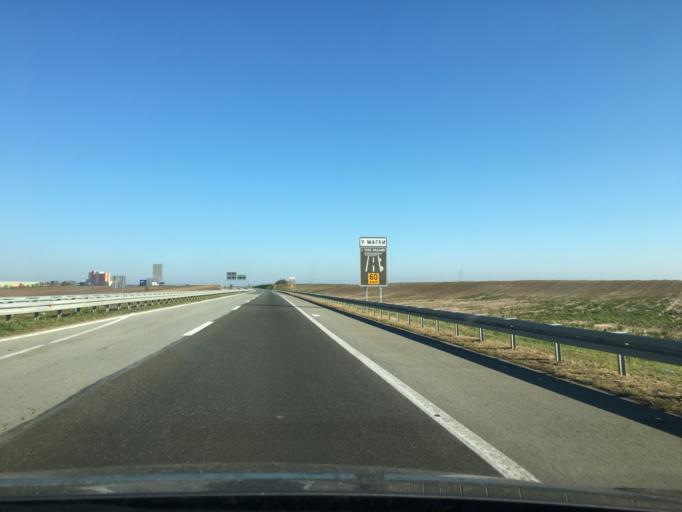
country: RS
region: Autonomna Pokrajina Vojvodina
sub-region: Severnobacki Okrug
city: Mali Igos
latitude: 45.6468
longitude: 19.7175
